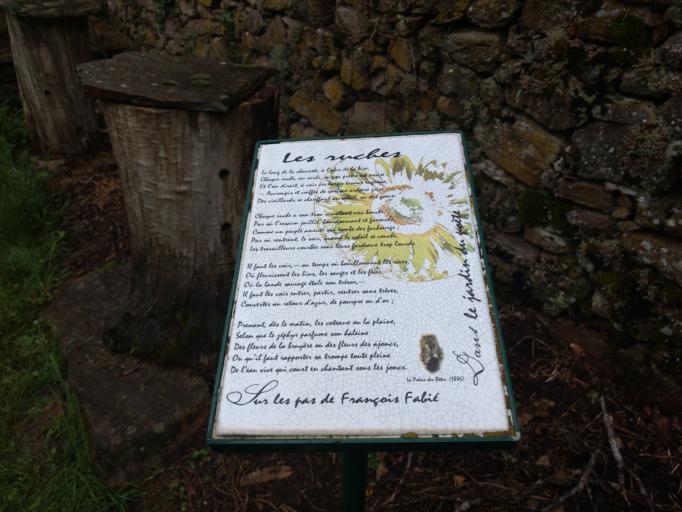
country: FR
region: Midi-Pyrenees
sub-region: Departement de l'Aveyron
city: Cassagnes-Begonhes
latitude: 44.1073
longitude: 2.6213
